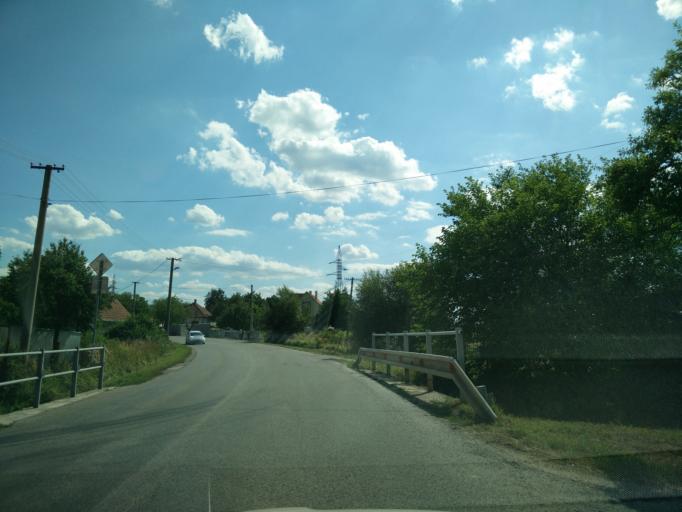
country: SK
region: Nitriansky
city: Prievidza
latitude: 48.7449
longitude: 18.6234
